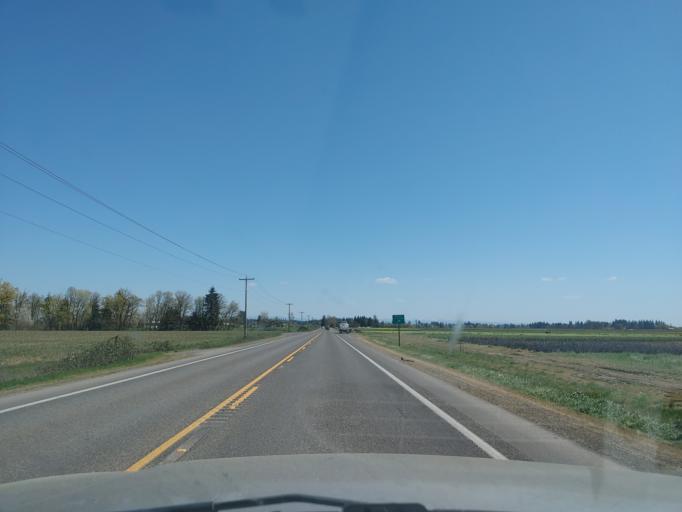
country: US
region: Oregon
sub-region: Yamhill County
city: Newberg
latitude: 45.2389
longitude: -122.9206
